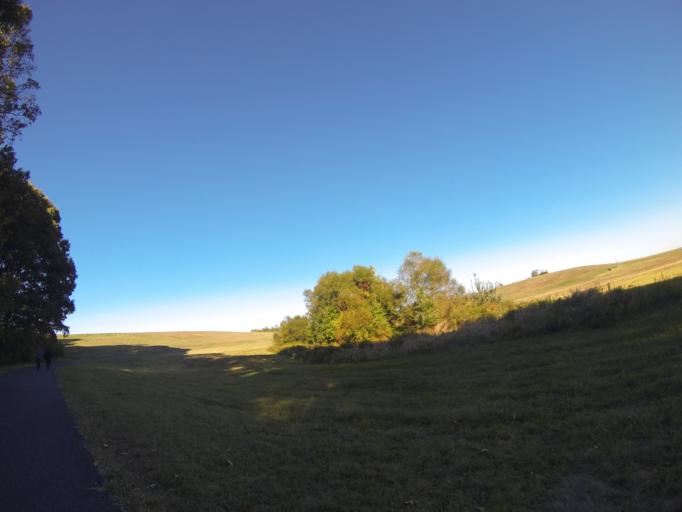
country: US
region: Maryland
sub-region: Anne Arundel County
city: Linthicum
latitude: 39.1939
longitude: -76.6704
